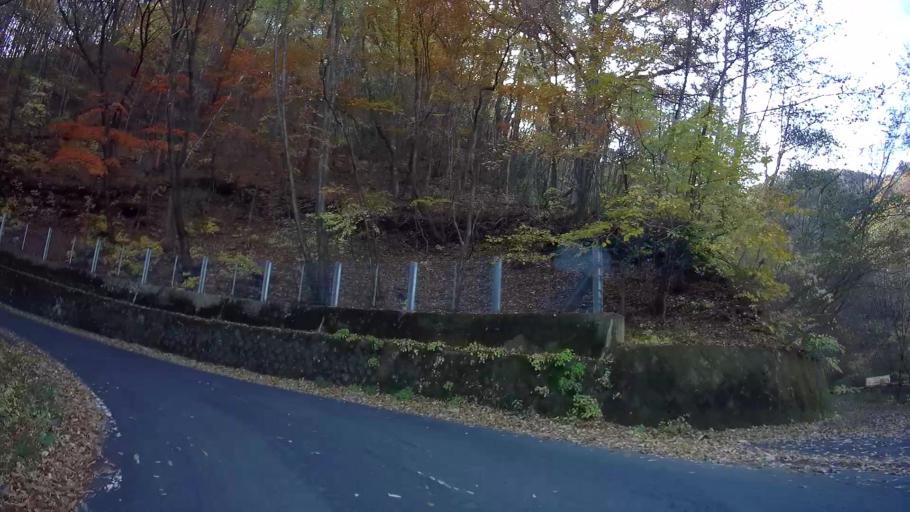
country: JP
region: Gunma
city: Nakanojomachi
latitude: 36.6222
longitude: 138.6352
